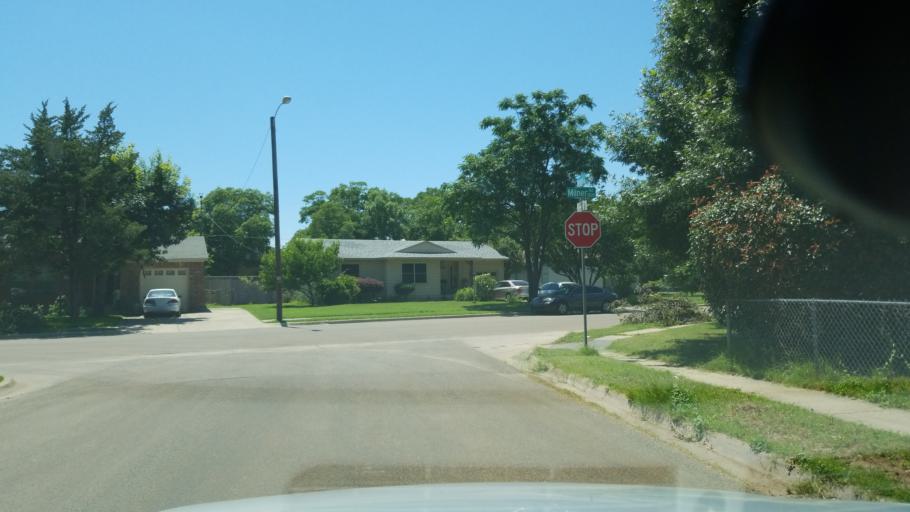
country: US
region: Texas
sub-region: Dallas County
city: Irving
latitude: 32.8305
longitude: -96.9324
